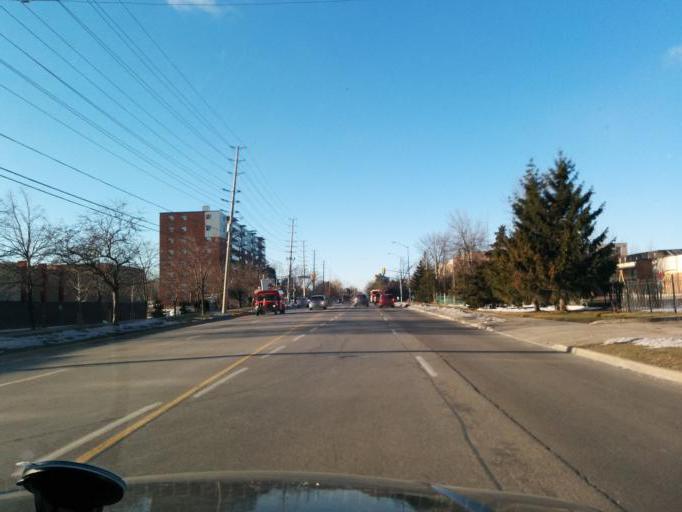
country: CA
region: Ontario
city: Mississauga
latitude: 43.5584
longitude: -79.6443
